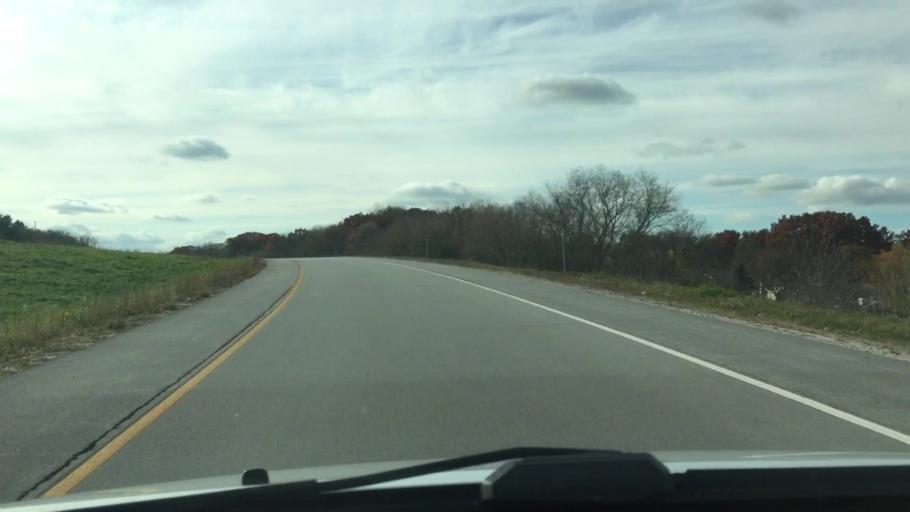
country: US
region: Wisconsin
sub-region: Waukesha County
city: Hartland
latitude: 43.1101
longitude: -88.3480
